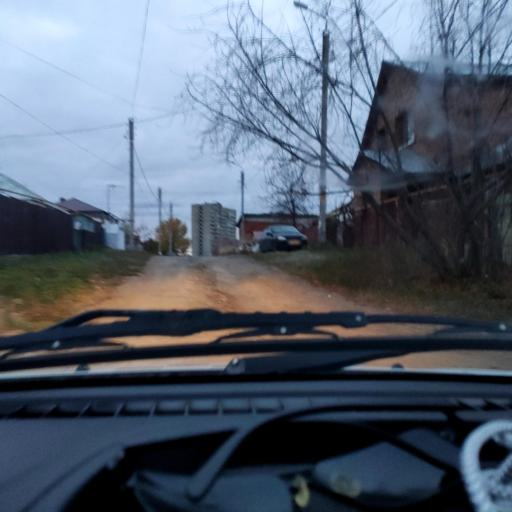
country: RU
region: Samara
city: Zhigulevsk
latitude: 53.4834
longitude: 49.5240
